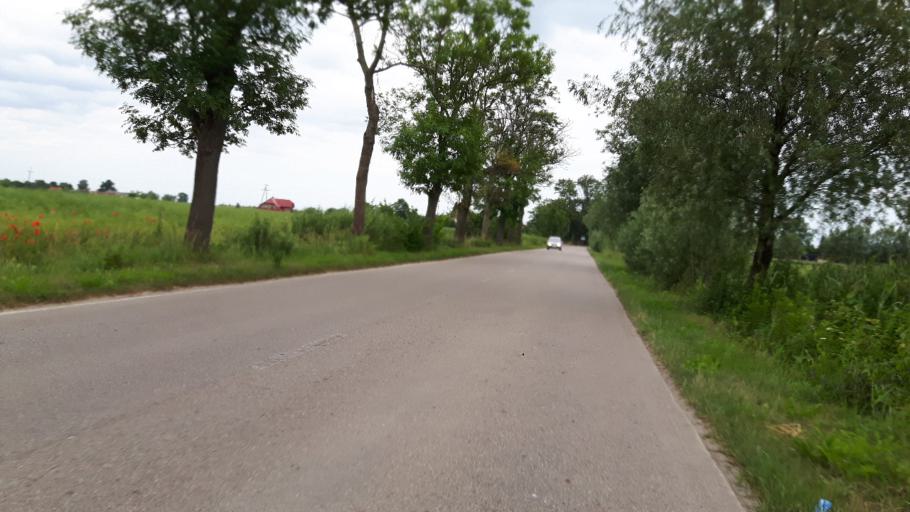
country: PL
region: Warmian-Masurian Voivodeship
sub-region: Powiat elblaski
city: Gronowo Elblaskie
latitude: 54.1931
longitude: 19.2952
